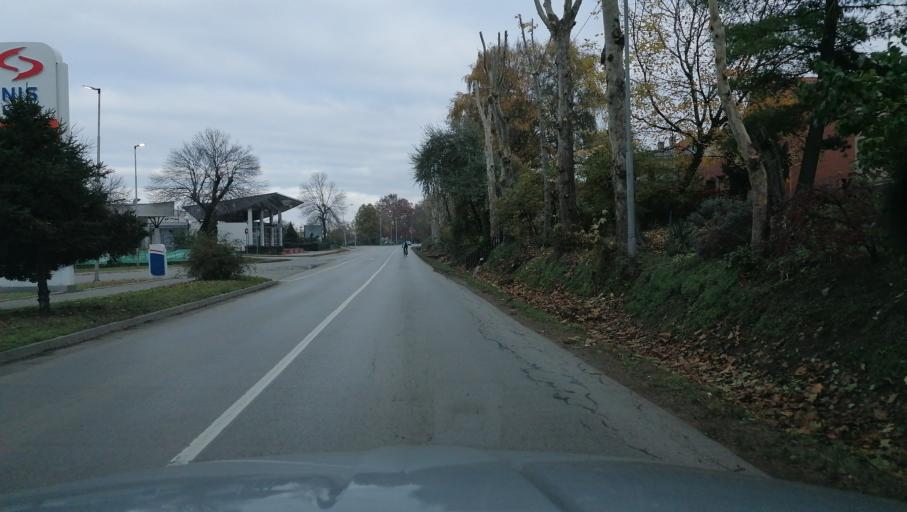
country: RS
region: Central Serbia
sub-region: Podunavski Okrug
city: Smederevo
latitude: 44.6635
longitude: 20.9085
